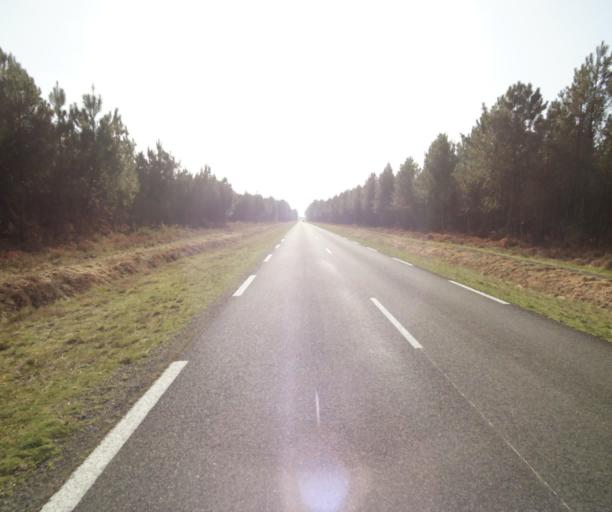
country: FR
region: Aquitaine
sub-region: Departement de la Gironde
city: Grignols
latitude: 44.1842
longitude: -0.1450
